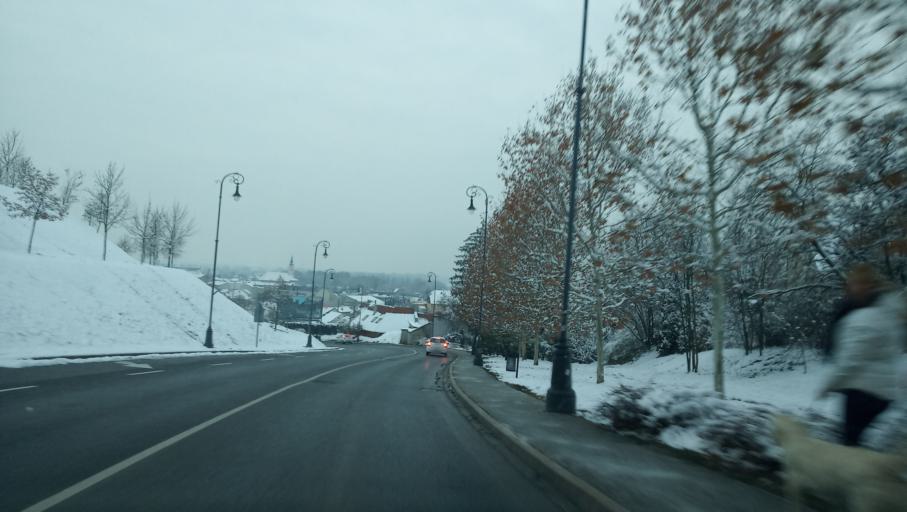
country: HU
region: Komarom-Esztergom
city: Esztergom
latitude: 47.7977
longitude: 18.7462
